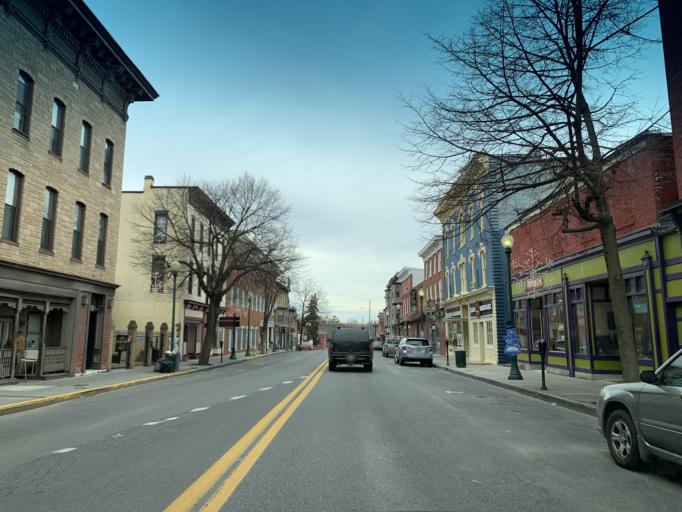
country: US
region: West Virginia
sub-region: Berkeley County
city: Martinsburg
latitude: 39.4589
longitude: -77.9631
